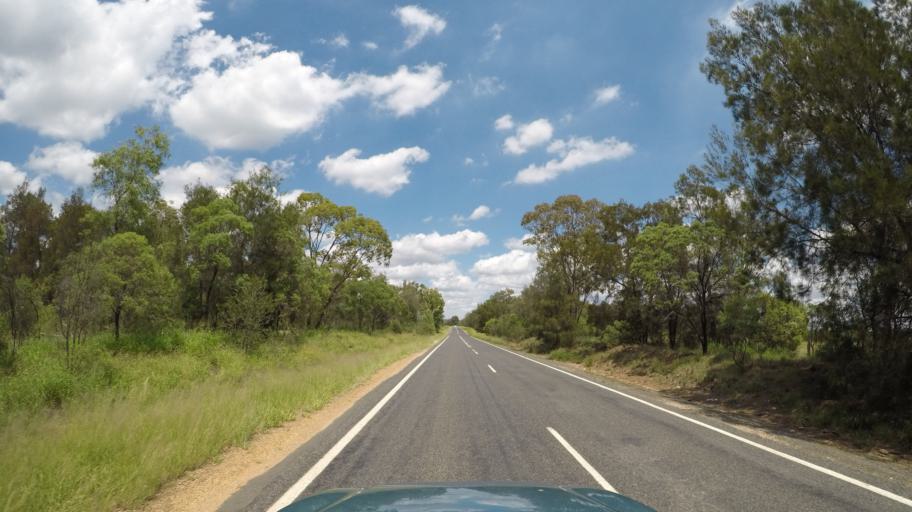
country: AU
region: Queensland
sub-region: Western Downs
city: Dalby
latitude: -27.9527
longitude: 151.1355
